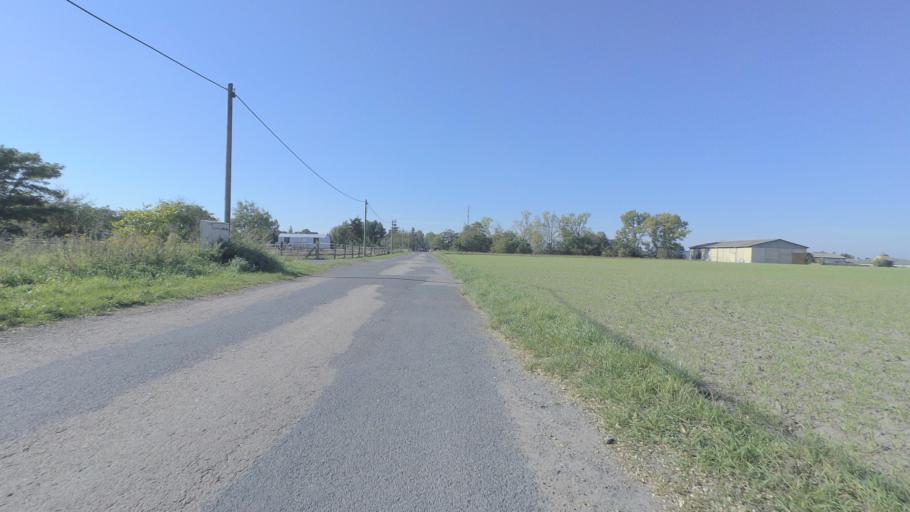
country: DE
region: Brandenburg
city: Rangsdorf
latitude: 52.2747
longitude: 13.3518
